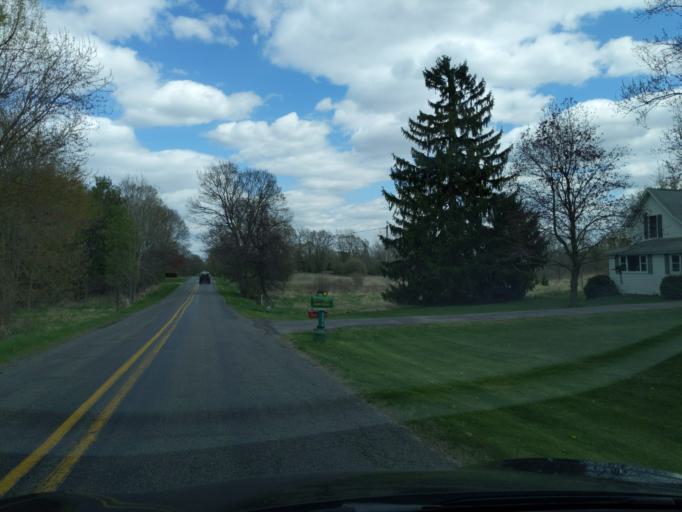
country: US
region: Michigan
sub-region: Eaton County
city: Dimondale
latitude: 42.6257
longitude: -84.5948
